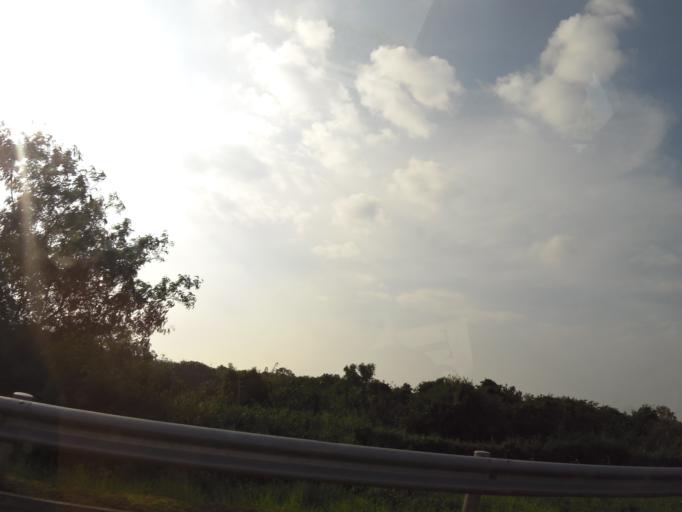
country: LK
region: Western
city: Ja Ela
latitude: 7.1030
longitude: 79.8777
